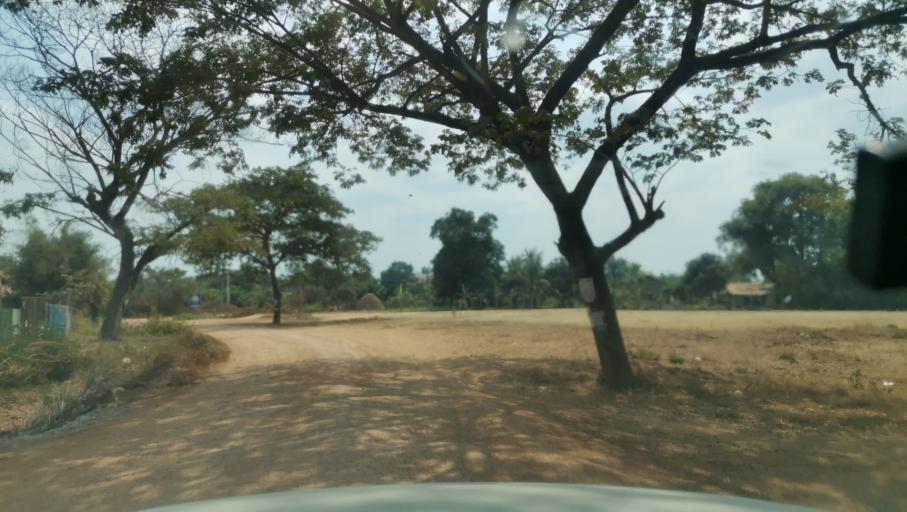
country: KH
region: Battambang
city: Battambang
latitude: 13.0571
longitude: 103.1692
